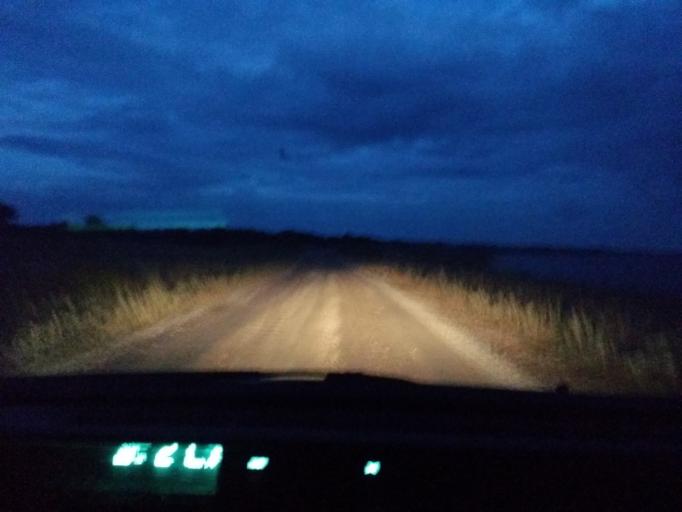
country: SE
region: Kalmar
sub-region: Borgholms Kommun
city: Borgholm
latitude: 57.1200
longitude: 16.8979
